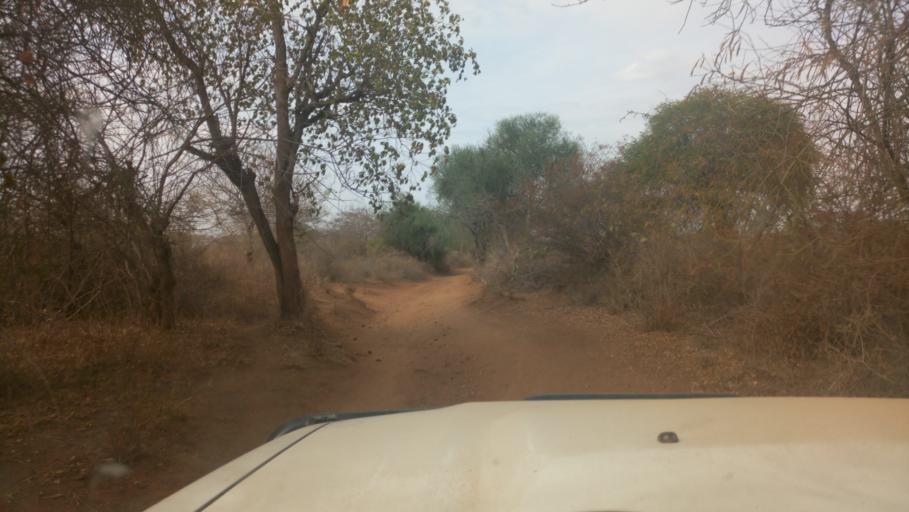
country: KE
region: Kitui
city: Kitui
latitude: -1.6359
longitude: 37.9230
